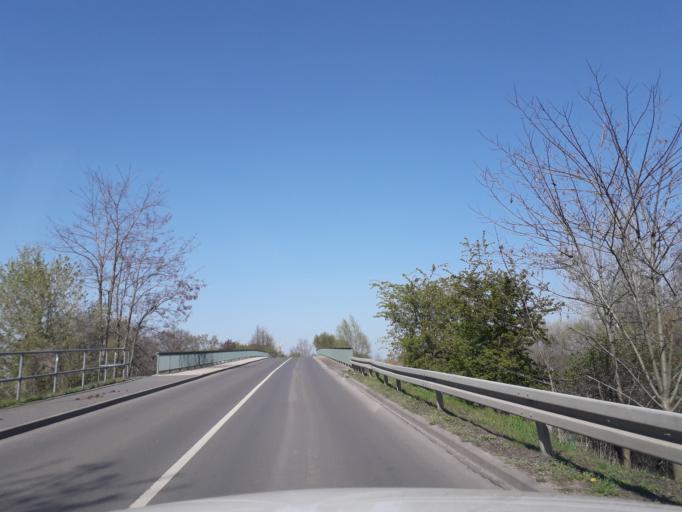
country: DE
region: Brandenburg
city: Dallgow-Doeberitz
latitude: 52.5446
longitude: 13.0370
